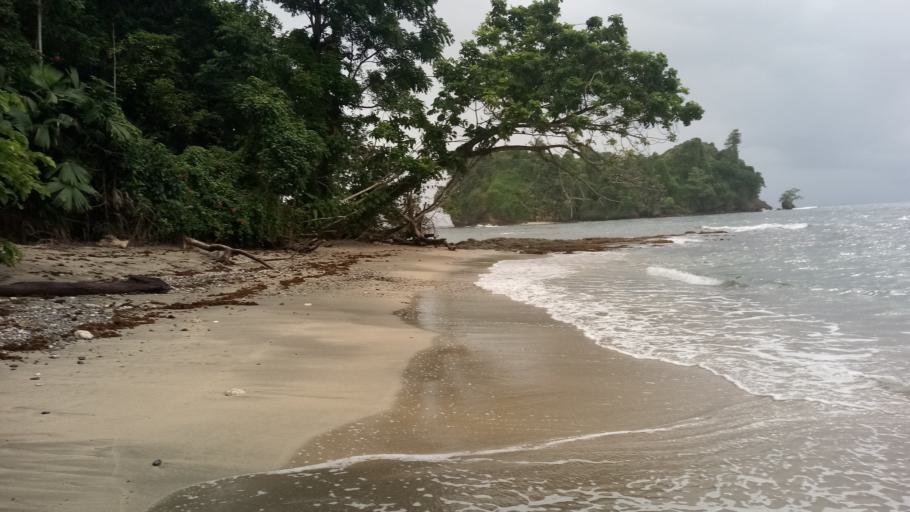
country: CR
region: Limon
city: Sixaola
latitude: 9.6290
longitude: -82.6196
